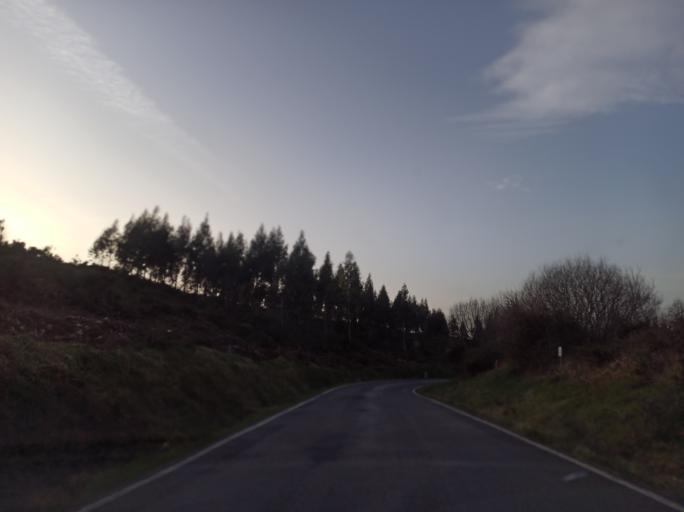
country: ES
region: Galicia
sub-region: Provincia da Coruna
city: Sobrado
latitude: 43.0367
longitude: -7.9444
